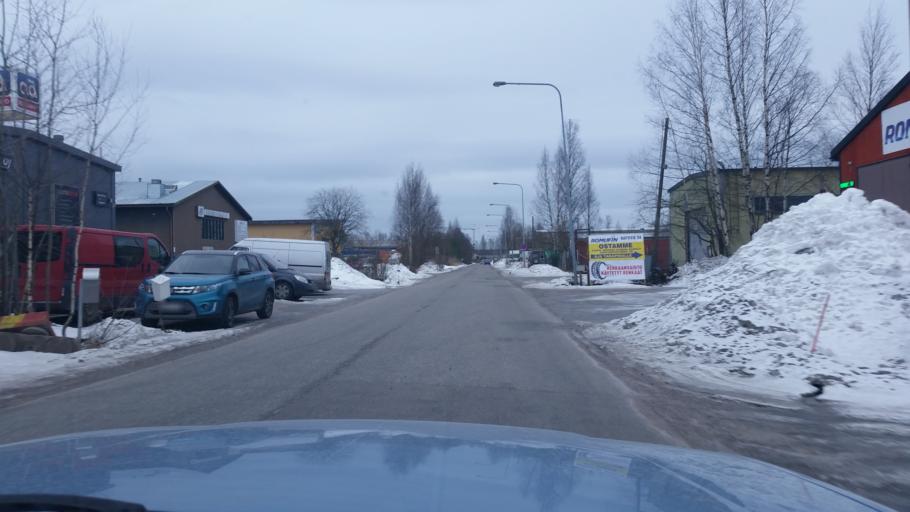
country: FI
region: Uusimaa
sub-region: Helsinki
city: Vantaa
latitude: 60.2616
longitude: 25.0544
